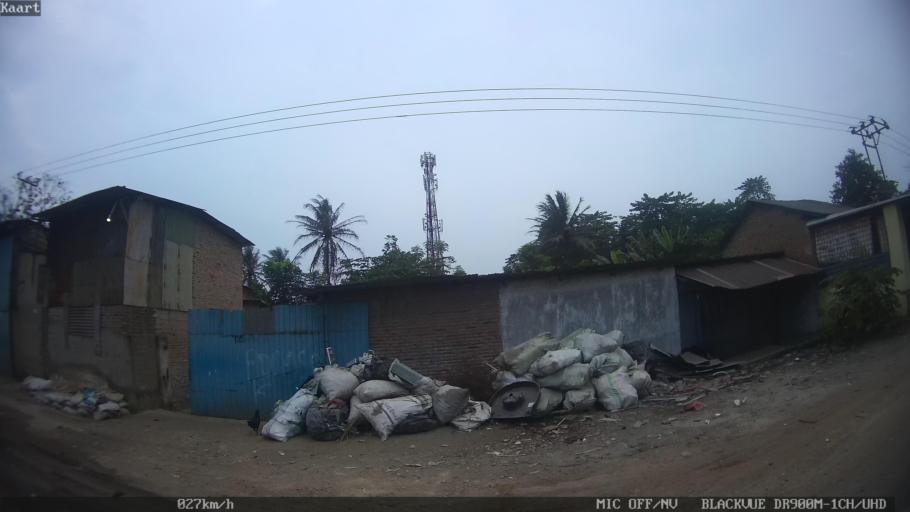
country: ID
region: Lampung
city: Panjang
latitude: -5.4315
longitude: 105.3256
